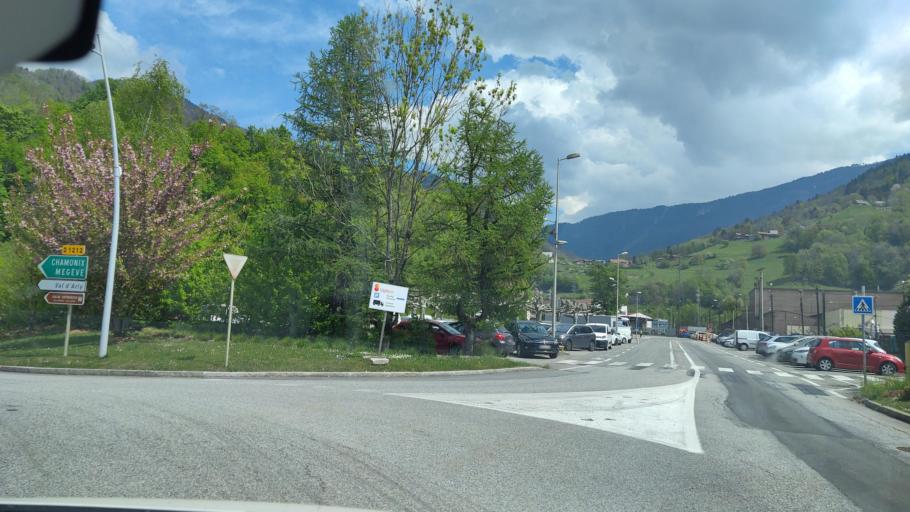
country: FR
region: Rhone-Alpes
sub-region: Departement de la Savoie
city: Ugine
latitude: 45.7463
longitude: 6.4263
